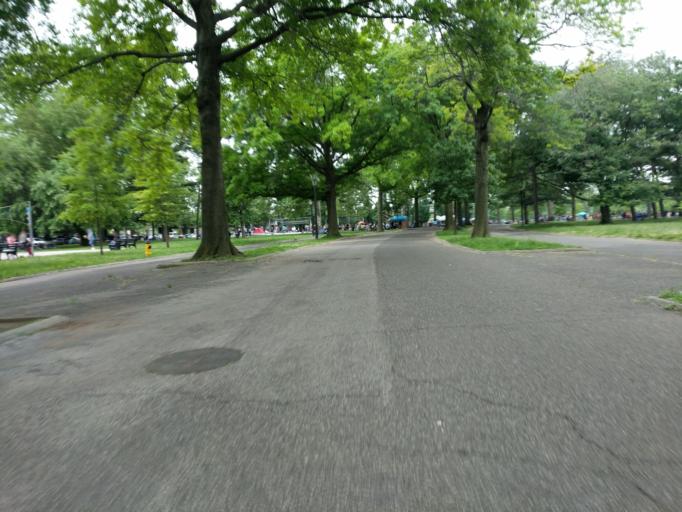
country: US
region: New York
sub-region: Queens County
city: Jamaica
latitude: 40.7482
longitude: -73.8359
